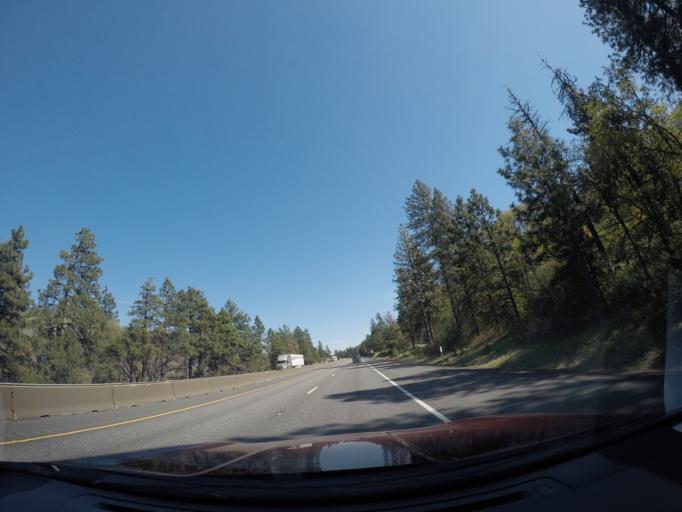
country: US
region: Oregon
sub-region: Wasco County
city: Chenoweth
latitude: 45.6707
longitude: -121.2570
